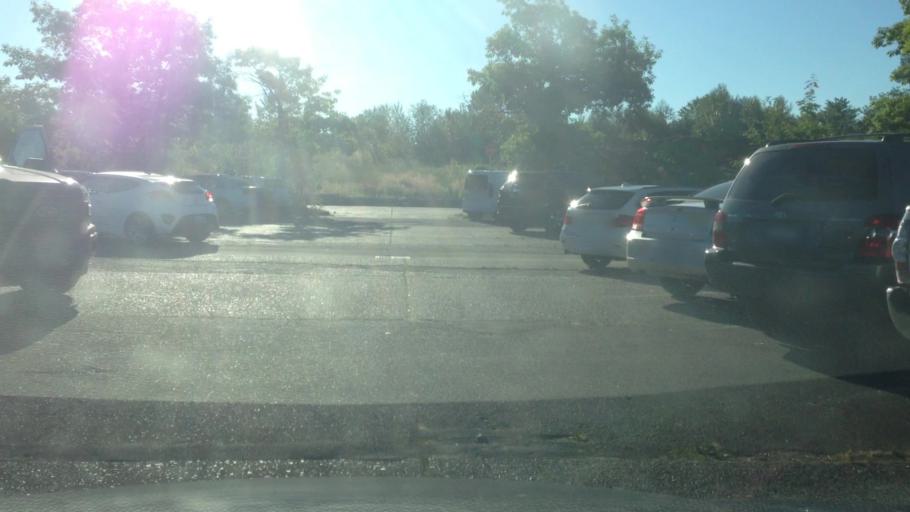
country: US
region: Washington
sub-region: King County
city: Kirkland
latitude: 47.6766
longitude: -122.2566
